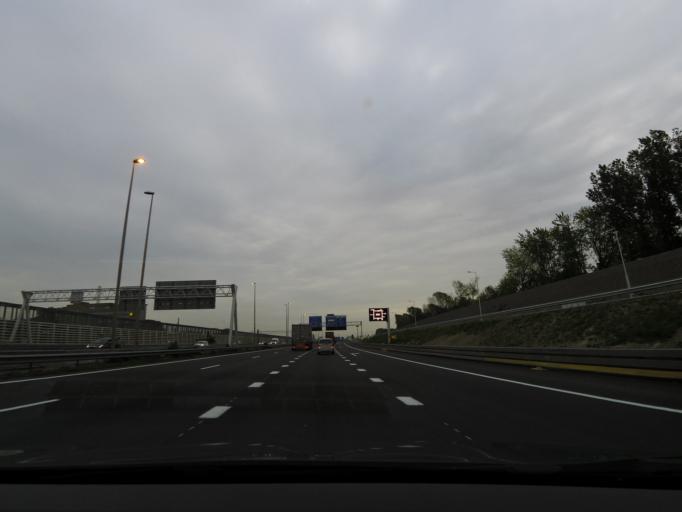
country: NL
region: South Holland
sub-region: Gemeente Spijkenisse
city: Spijkenisse
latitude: 51.8750
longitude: 4.3499
